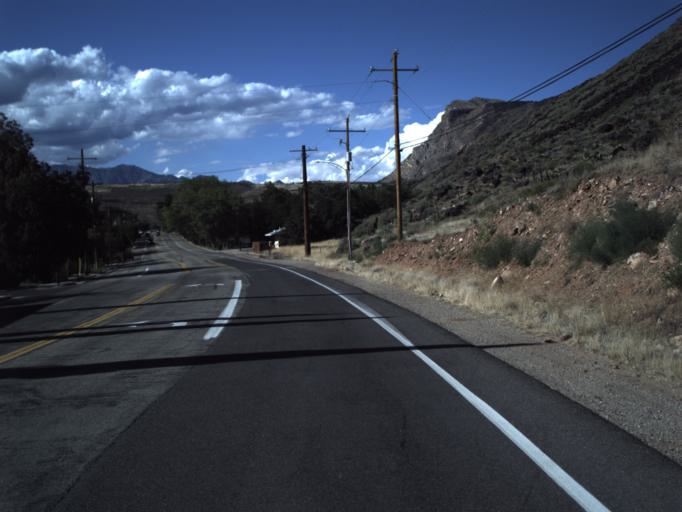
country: US
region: Utah
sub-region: Washington County
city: Toquerville
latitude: 37.2487
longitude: -113.2837
